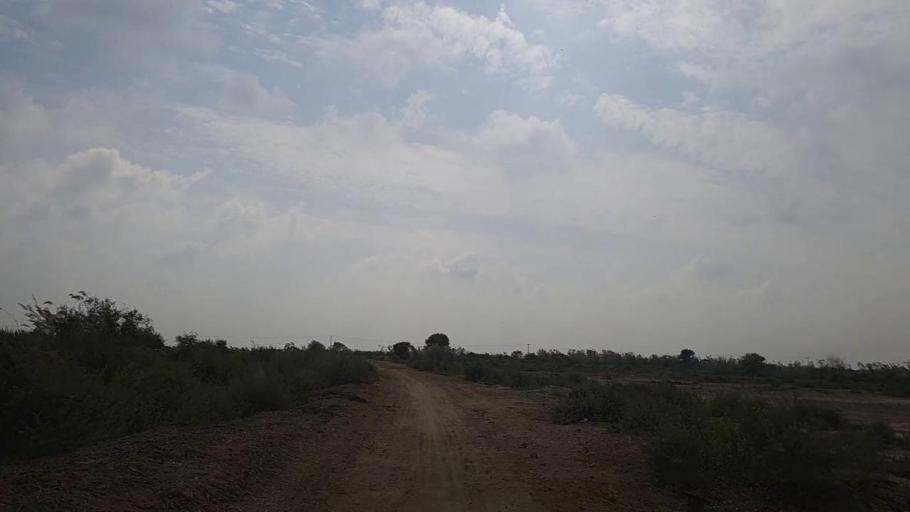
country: PK
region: Sindh
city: Mirpur Batoro
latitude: 24.6044
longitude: 68.1394
